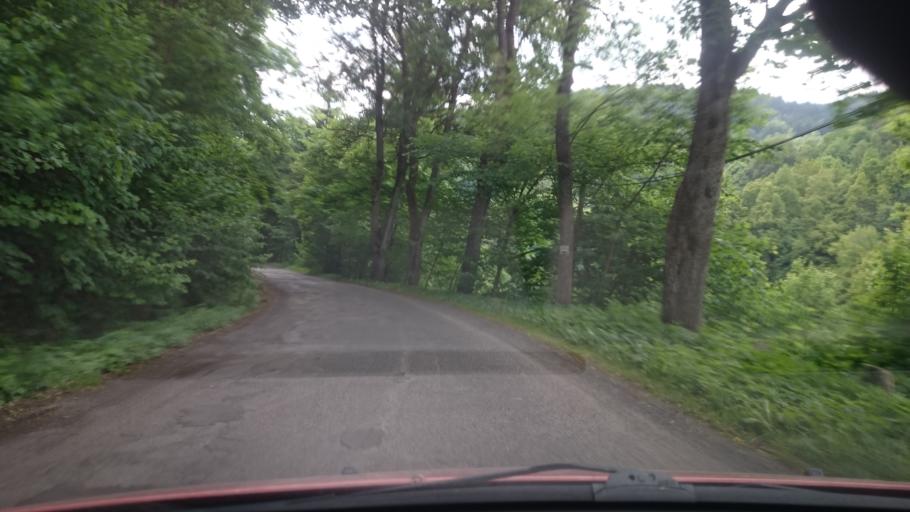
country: PL
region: Lower Silesian Voivodeship
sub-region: Powiat klodzki
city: Bystrzyca Klodzka
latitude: 50.3025
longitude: 16.5592
